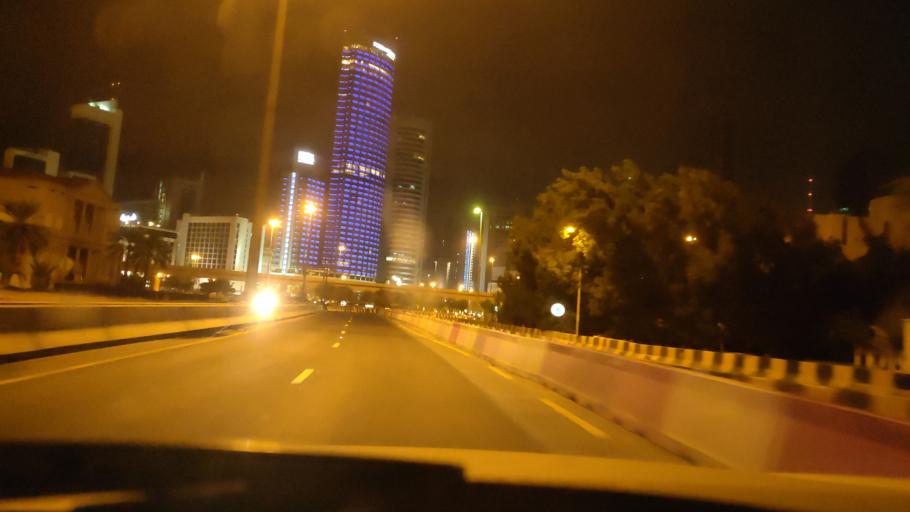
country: KW
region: Al Asimah
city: Ash Shamiyah
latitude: 29.3578
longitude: 47.9627
